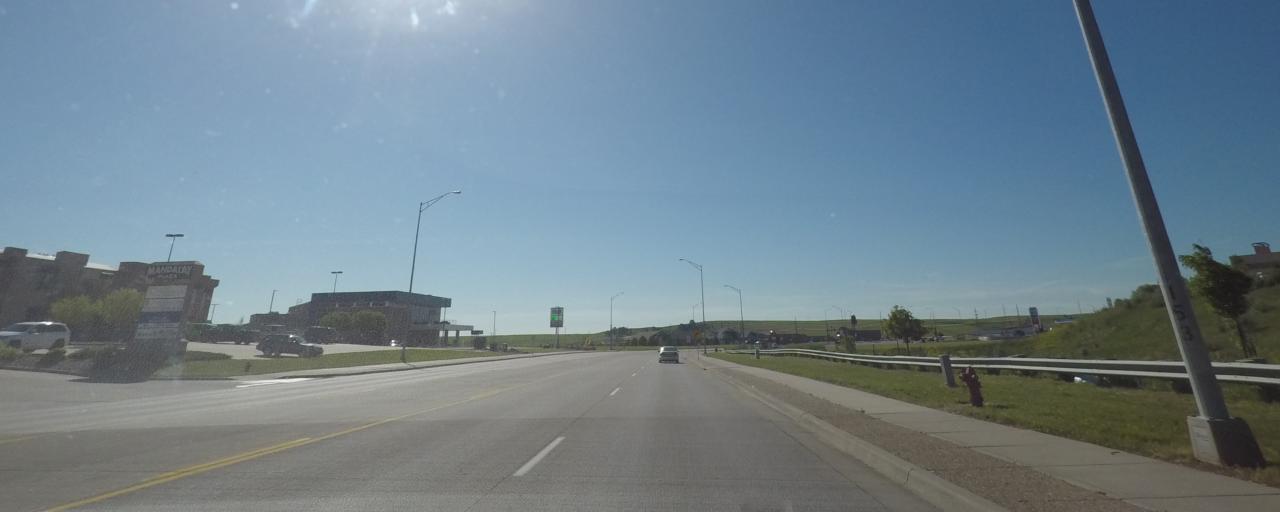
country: US
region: South Dakota
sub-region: Pennington County
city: Rapid City
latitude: 44.0351
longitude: -103.2150
